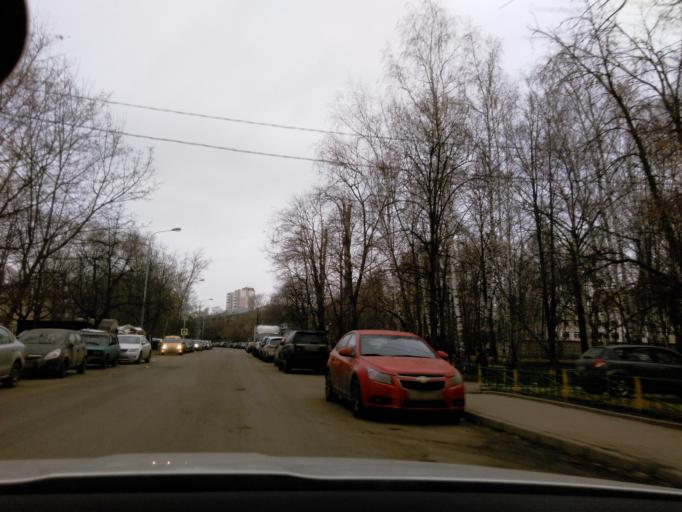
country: RU
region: Moskovskaya
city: Koptevo
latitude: 55.8179
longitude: 37.5305
